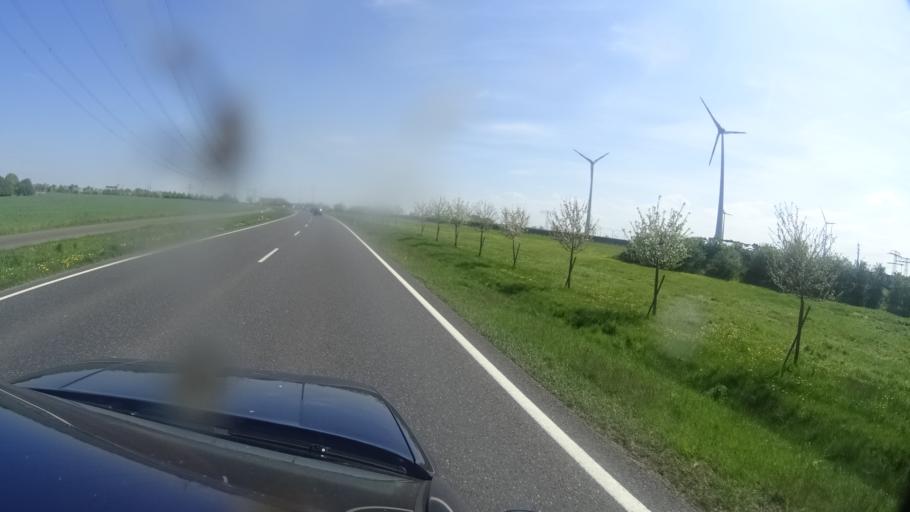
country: DE
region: Brandenburg
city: Nauen
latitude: 52.5959
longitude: 12.8581
